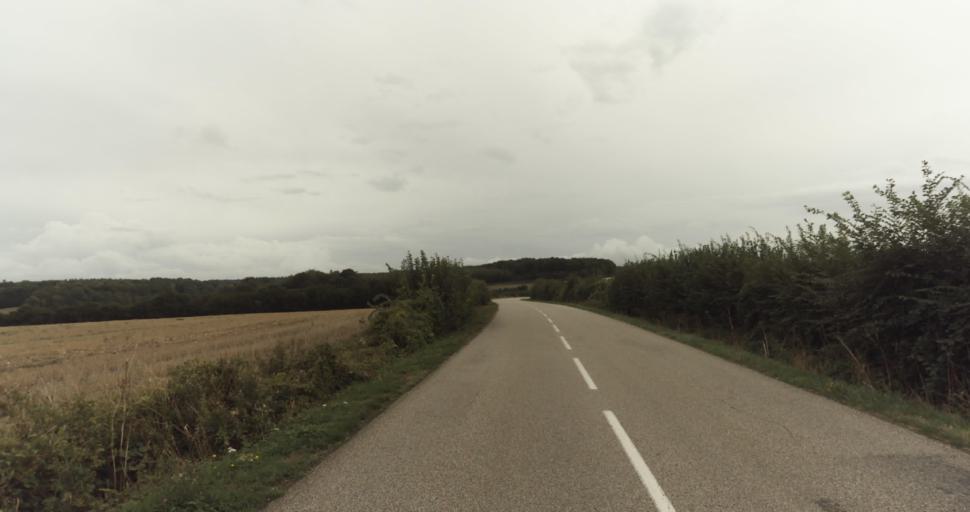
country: FR
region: Lower Normandy
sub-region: Departement de l'Orne
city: Gace
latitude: 48.8001
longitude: 0.3172
